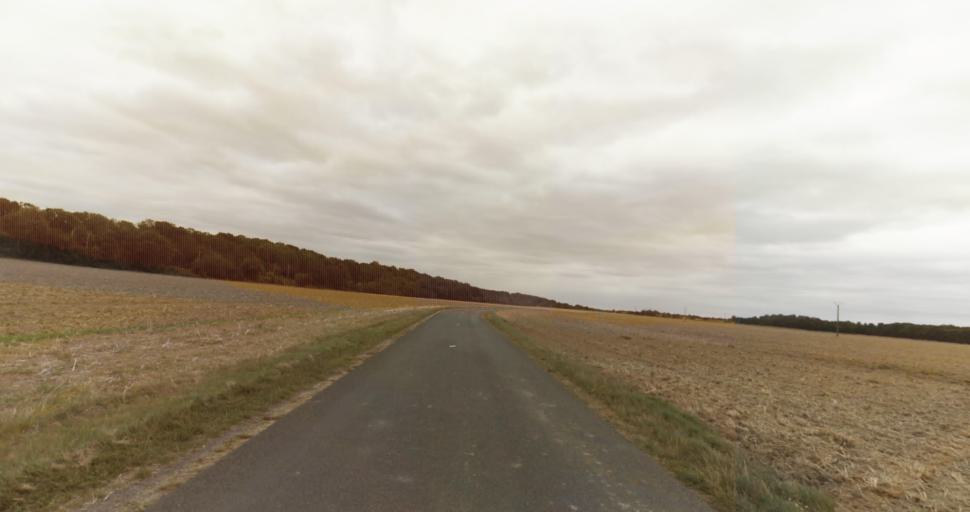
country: FR
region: Haute-Normandie
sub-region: Departement de l'Eure
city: Evreux
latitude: 49.0014
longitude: 1.2039
